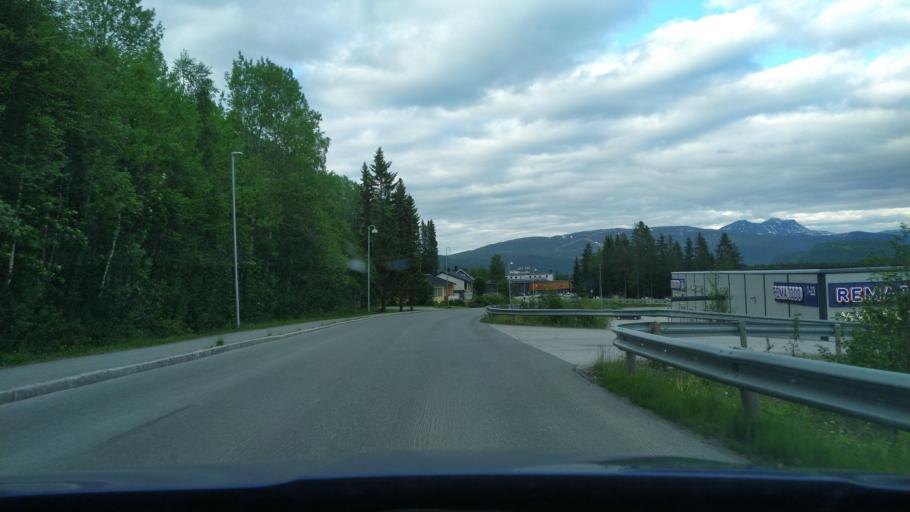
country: NO
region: Troms
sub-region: Malselv
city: Moen
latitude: 69.0641
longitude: 18.5028
